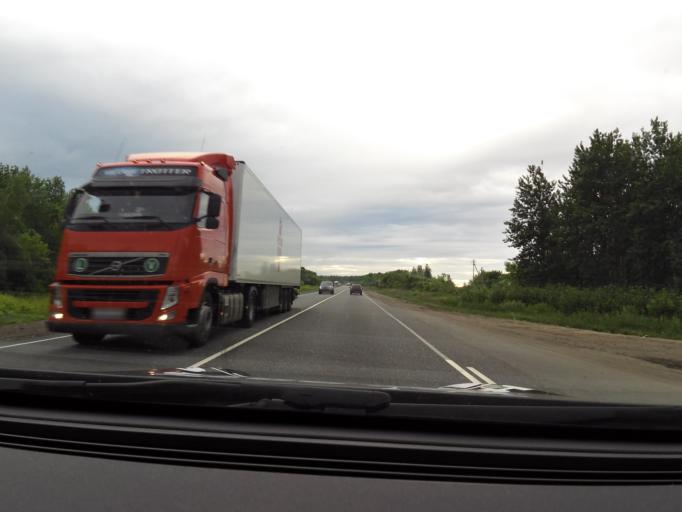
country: RU
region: Chuvashia
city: Kozlovka
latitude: 55.7925
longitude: 48.1389
